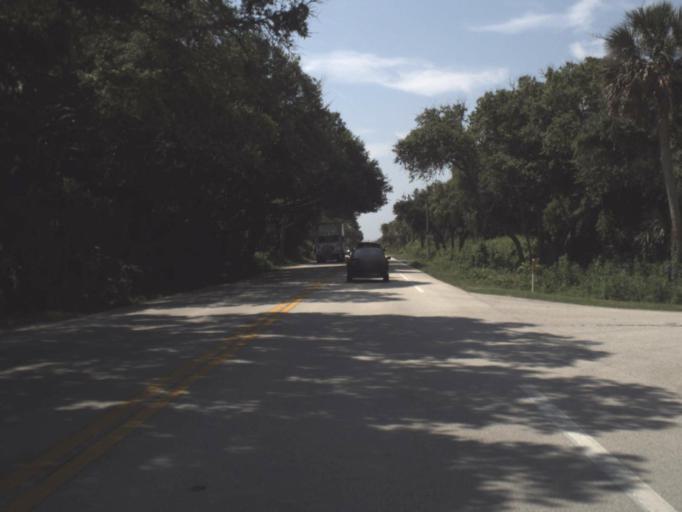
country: US
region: Florida
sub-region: Saint Johns County
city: Palm Valley
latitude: 30.1572
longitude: -81.3559
